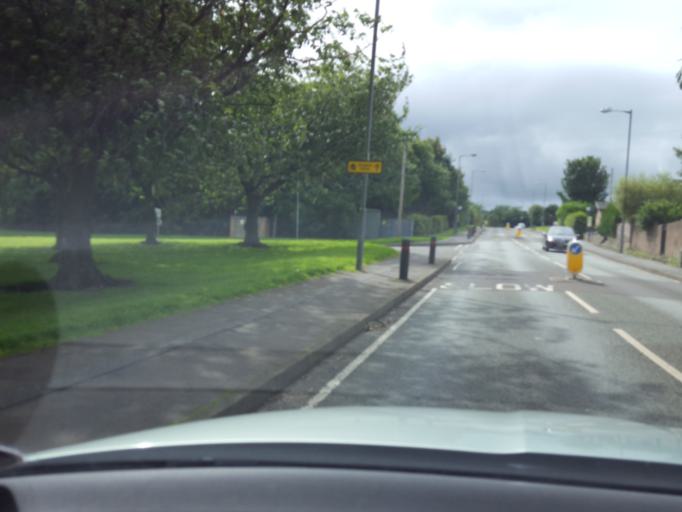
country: GB
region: Scotland
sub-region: Falkirk
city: Bo'ness
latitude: 56.0082
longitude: -3.5999
